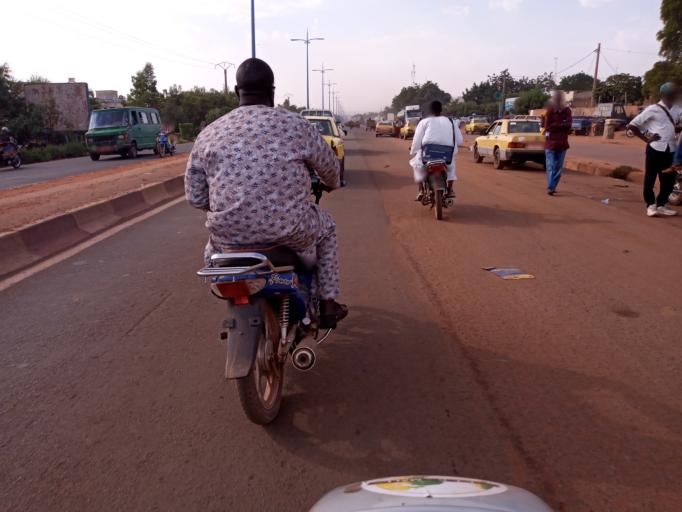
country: ML
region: Bamako
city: Bamako
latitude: 12.5856
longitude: -7.9446
